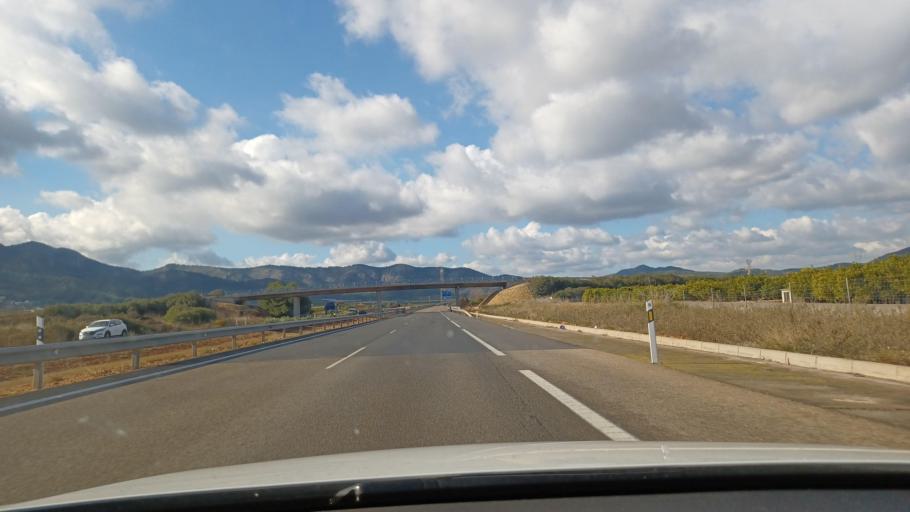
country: ES
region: Valencia
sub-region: Provincia de Castello
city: Villavieja
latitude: 39.8679
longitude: -0.1785
